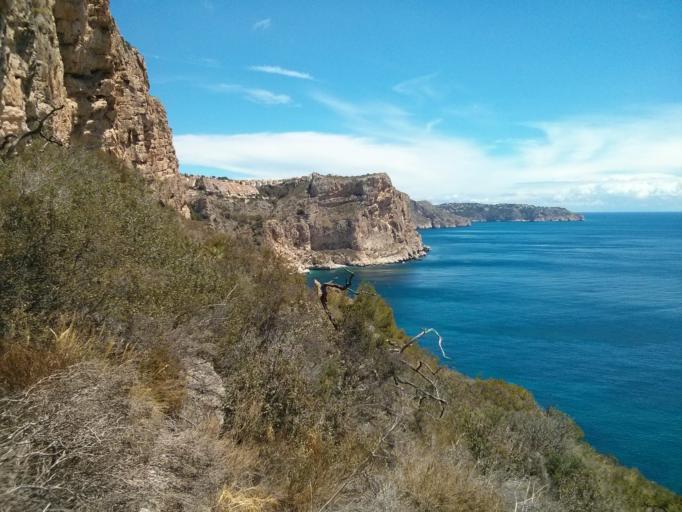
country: ES
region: Valencia
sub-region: Provincia de Alicante
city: Moraira
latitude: 38.7049
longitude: 0.1631
